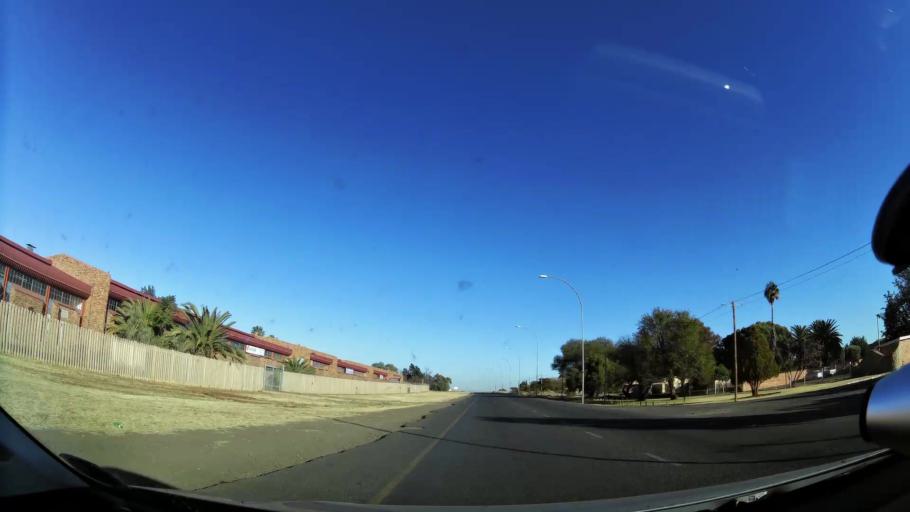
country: ZA
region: Northern Cape
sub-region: Frances Baard District Municipality
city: Kimberley
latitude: -28.7432
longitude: 24.7253
